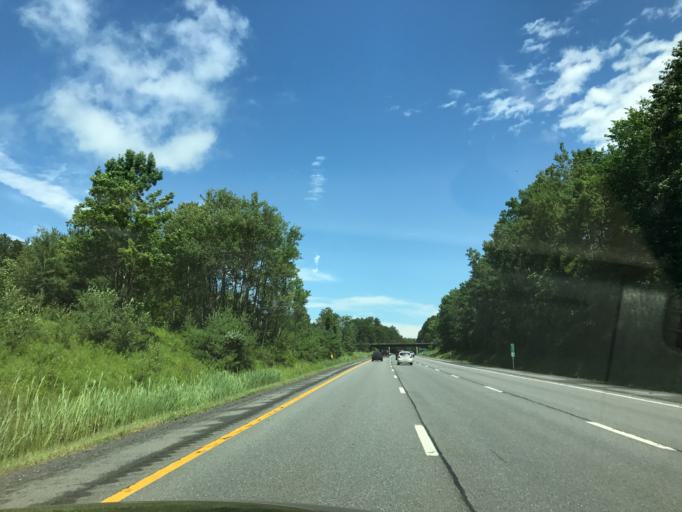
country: US
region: New York
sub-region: Warren County
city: West Glens Falls
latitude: 43.1877
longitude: -73.7053
